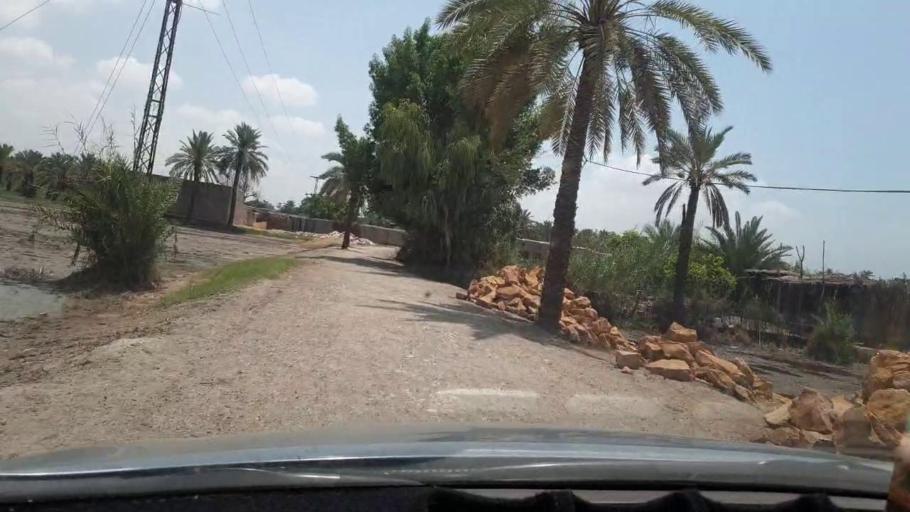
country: PK
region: Sindh
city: Khairpur
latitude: 27.4433
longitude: 68.7919
